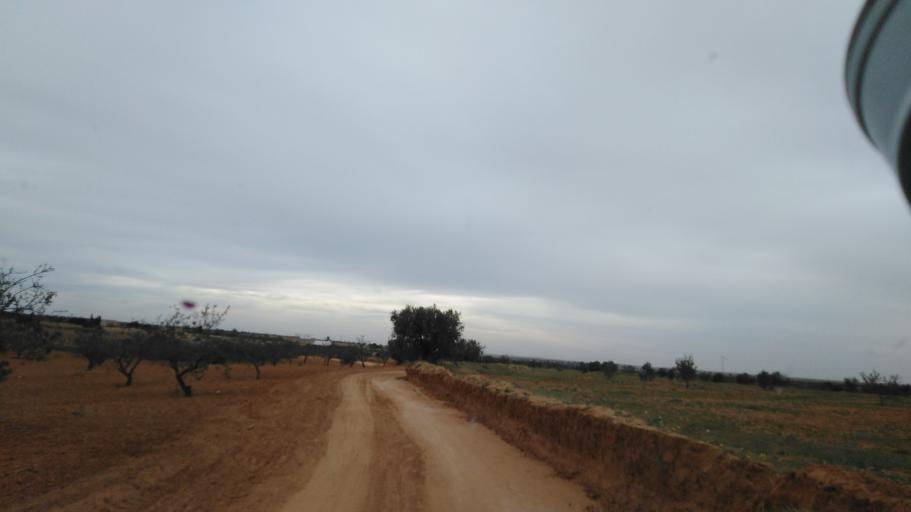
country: TN
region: Safaqis
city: Bi'r `Ali Bin Khalifah
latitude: 34.7692
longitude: 10.3747
